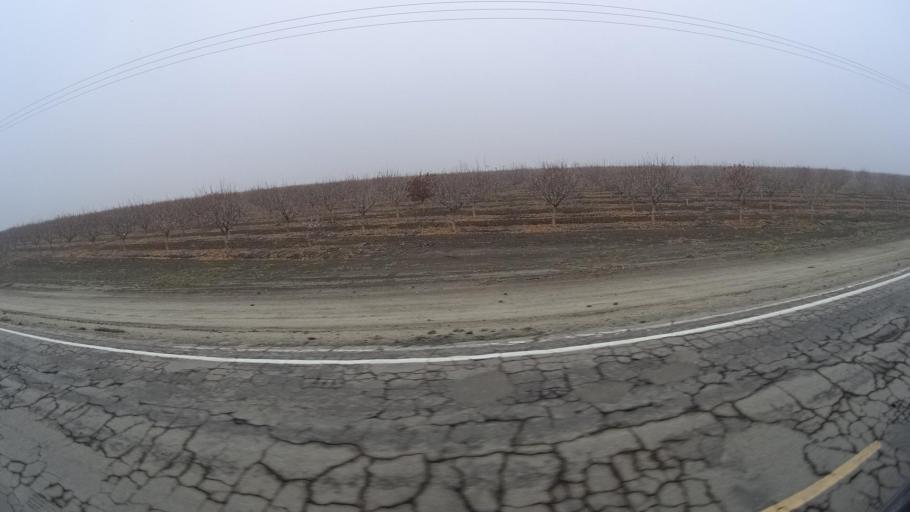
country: US
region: California
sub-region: Kern County
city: Lost Hills
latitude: 35.5156
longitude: -119.6161
